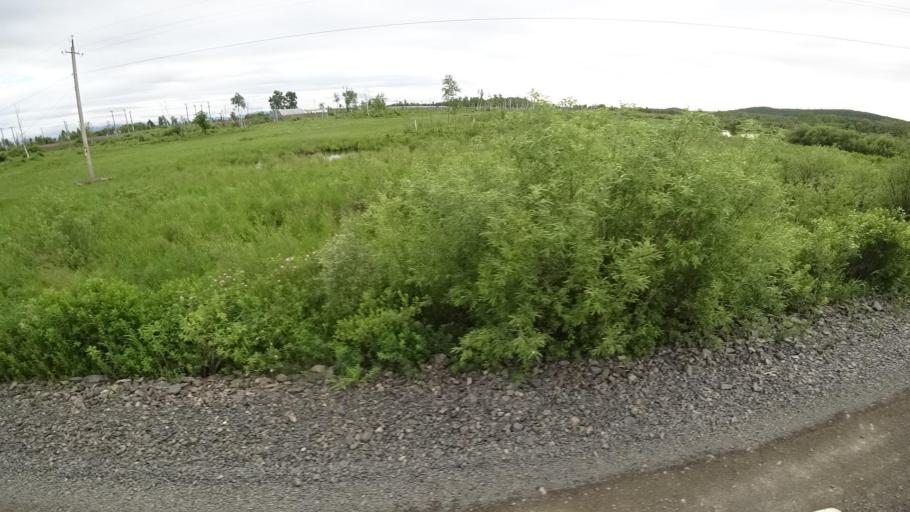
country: RU
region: Khabarovsk Krai
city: Amursk
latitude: 49.9024
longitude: 136.1459
